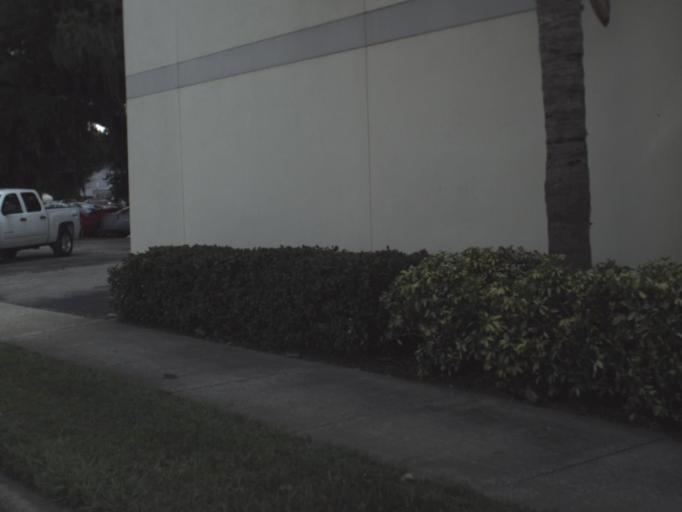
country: US
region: Florida
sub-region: Hillsborough County
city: Brandon
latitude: 27.9376
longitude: -82.2830
